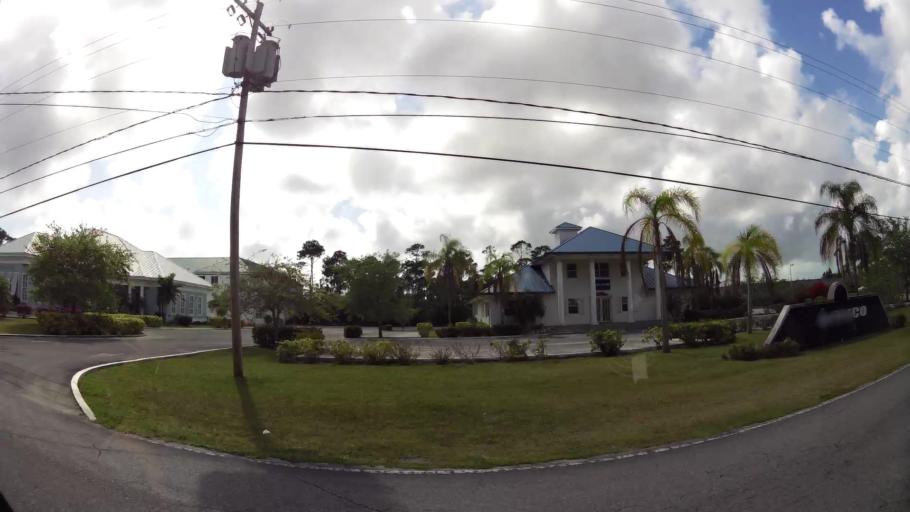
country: BS
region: Freeport
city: Freeport
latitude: 26.5246
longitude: -78.6972
